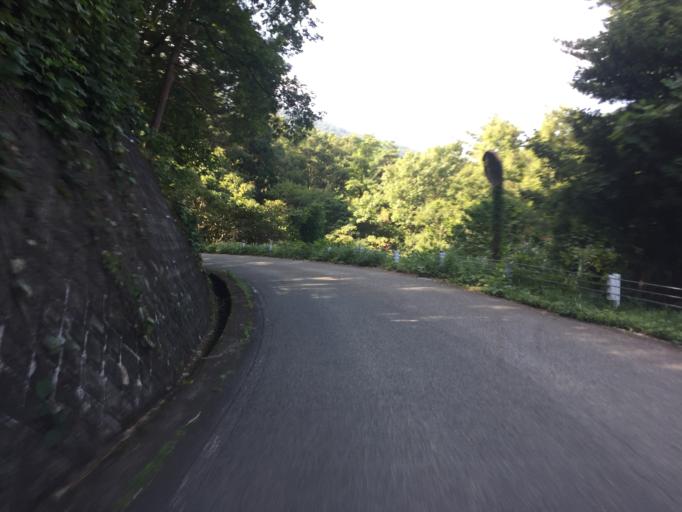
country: JP
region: Fukushima
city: Inawashiro
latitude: 37.4874
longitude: 139.9620
